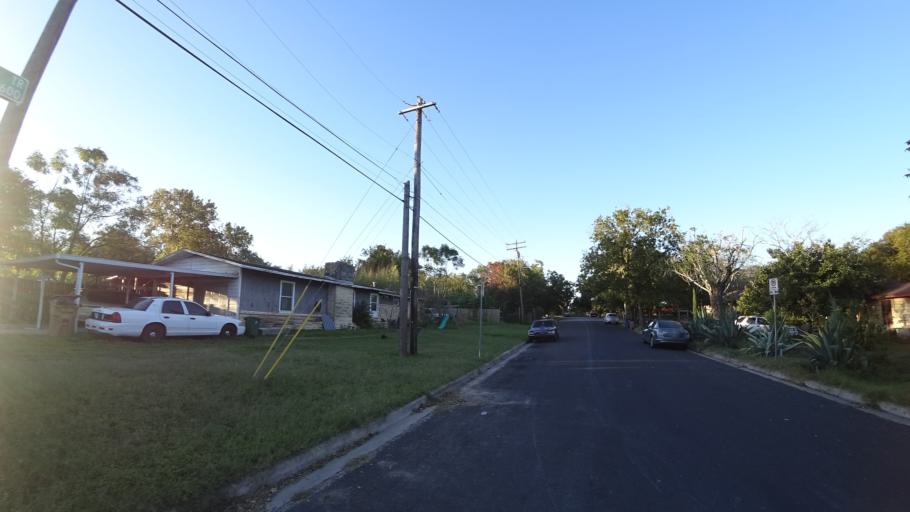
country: US
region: Texas
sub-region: Travis County
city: Austin
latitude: 30.2914
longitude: -97.6829
